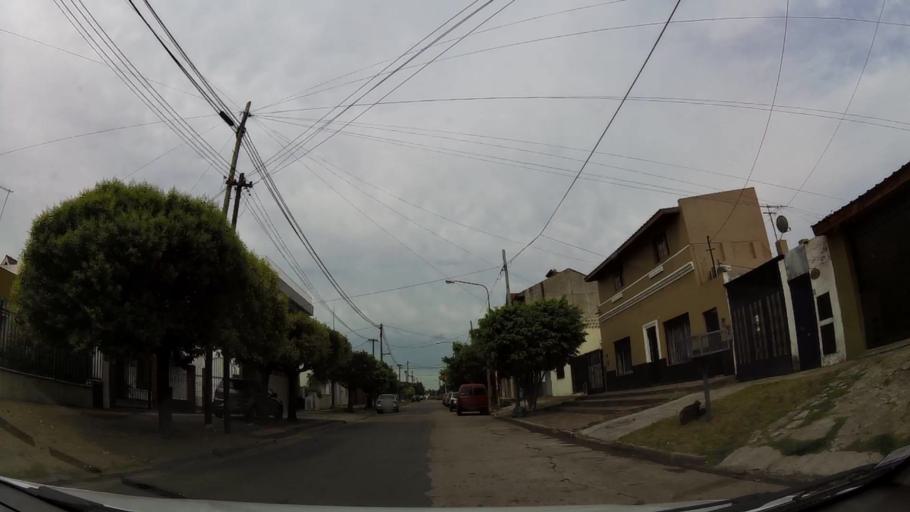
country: AR
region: Buenos Aires F.D.
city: Villa Lugano
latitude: -34.6969
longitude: -58.5147
